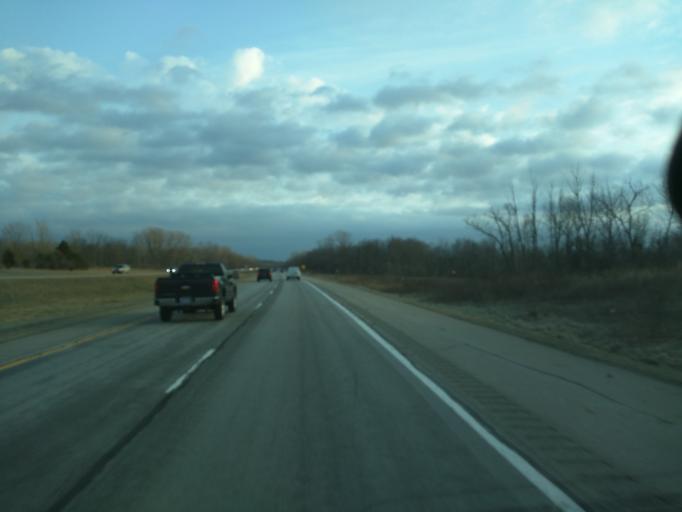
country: US
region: Michigan
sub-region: Ingham County
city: Holt
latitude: 42.6393
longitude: -84.4788
